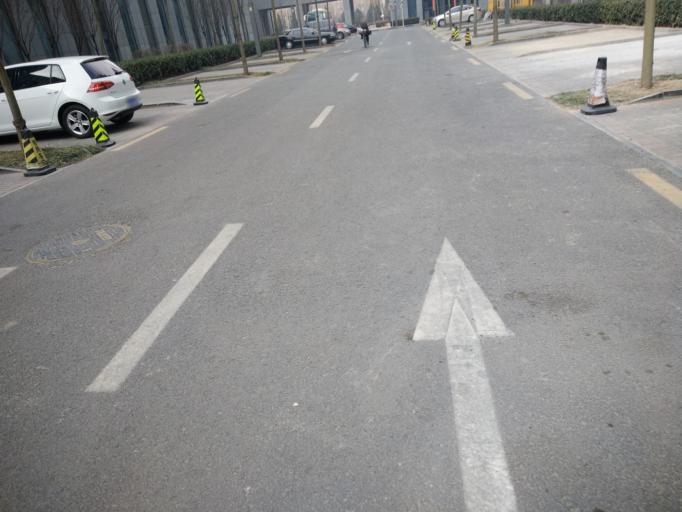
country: CN
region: Beijing
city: Jiugong
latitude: 39.7613
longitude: 116.5090
